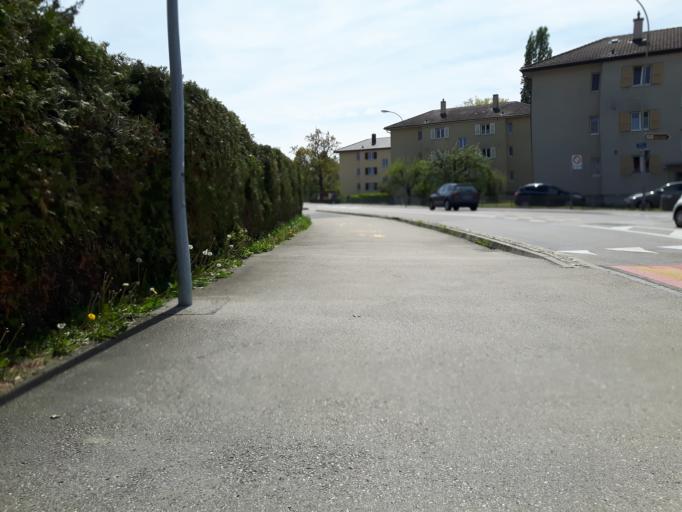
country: CH
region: Neuchatel
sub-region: Boudry District
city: Cortaillod
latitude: 46.9539
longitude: 6.8536
